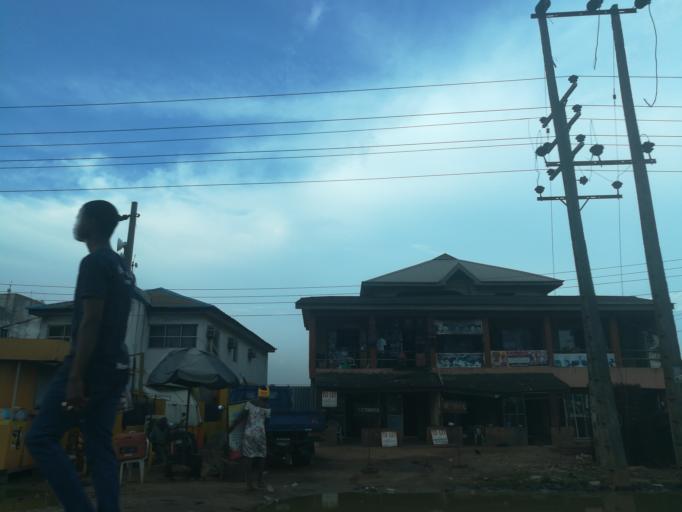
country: NG
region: Lagos
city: Ikorodu
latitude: 6.6237
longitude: 3.4966
